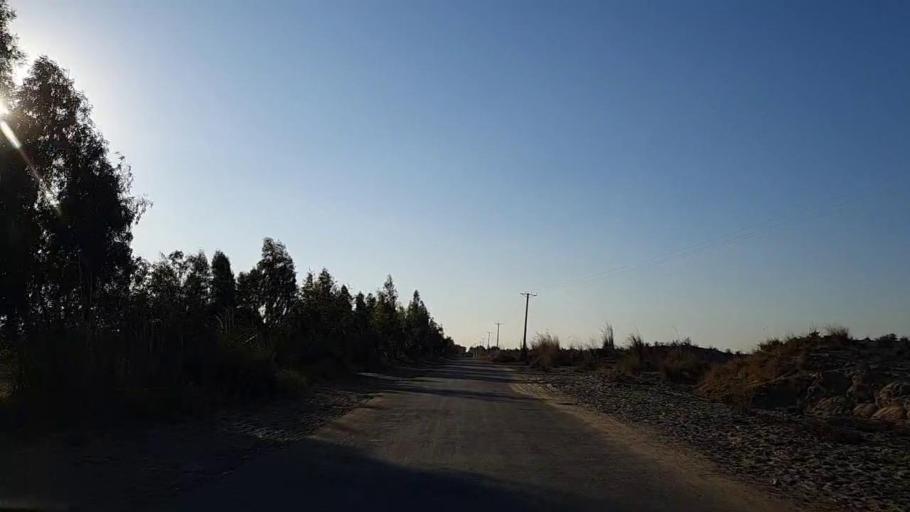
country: PK
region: Sindh
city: Khadro
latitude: 26.2790
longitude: 68.9089
